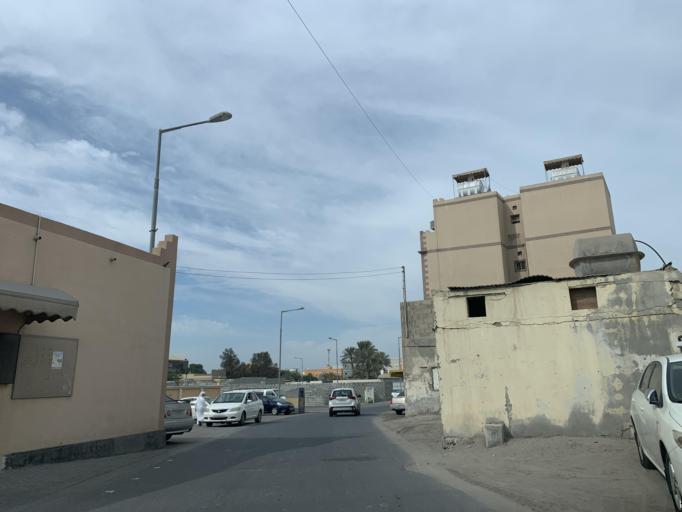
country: BH
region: Central Governorate
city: Madinat Hamad
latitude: 26.1144
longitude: 50.4802
